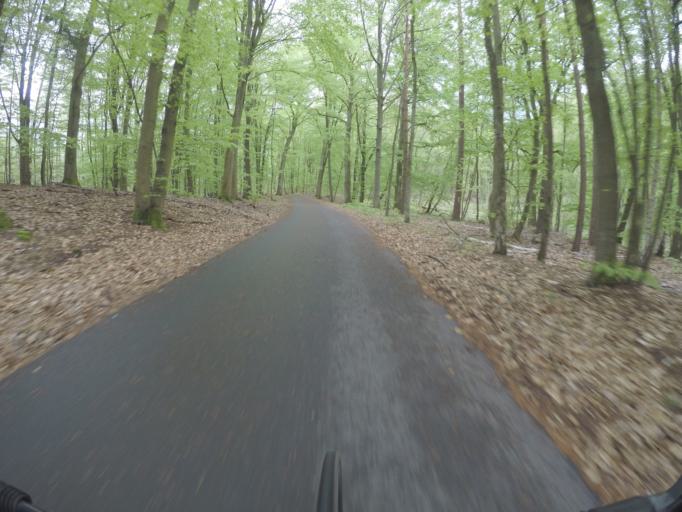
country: DE
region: Brandenburg
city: Marienwerder
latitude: 52.8645
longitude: 13.6142
